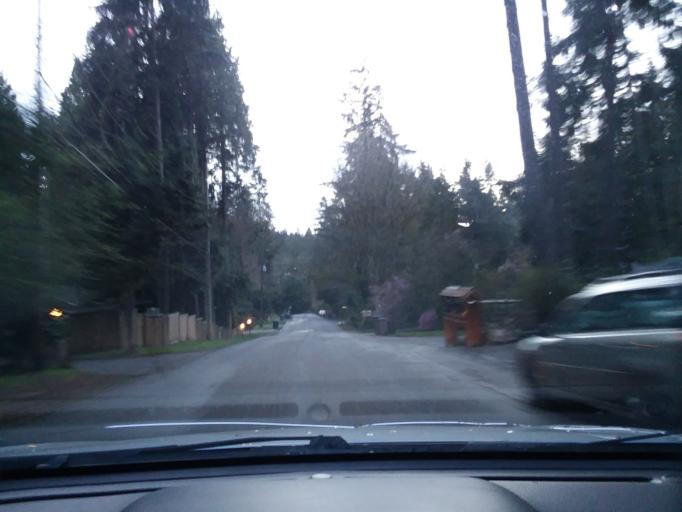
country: US
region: Washington
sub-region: King County
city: Lake Forest Park
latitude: 47.7610
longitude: -122.2951
